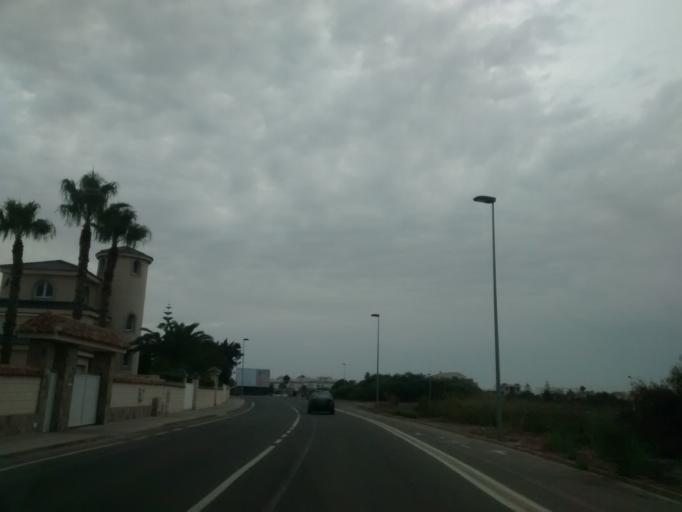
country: ES
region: Murcia
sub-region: Murcia
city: San Pedro del Pinatar
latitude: 37.7784
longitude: -0.7485
